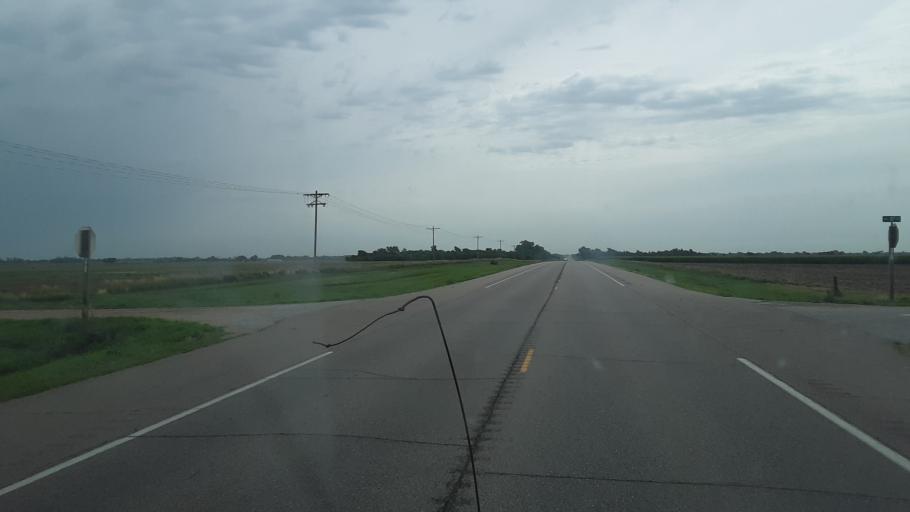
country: US
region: Kansas
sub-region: Stafford County
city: Saint John
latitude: 37.9560
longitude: -98.8588
